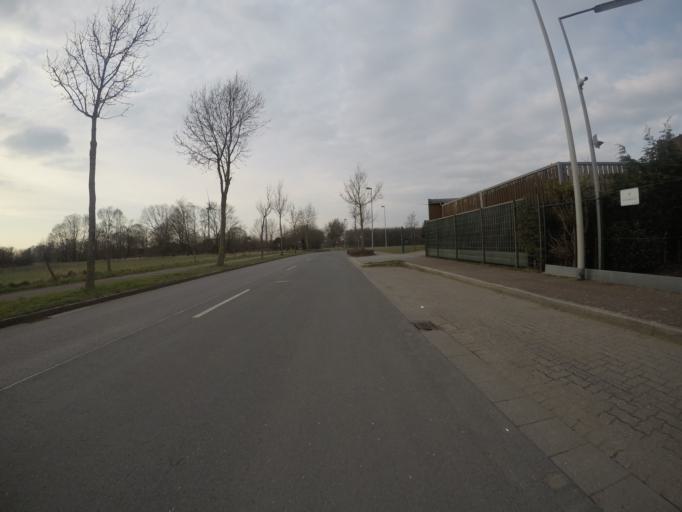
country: DE
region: North Rhine-Westphalia
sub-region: Regierungsbezirk Munster
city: Isselburg
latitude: 51.8147
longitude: 6.5387
